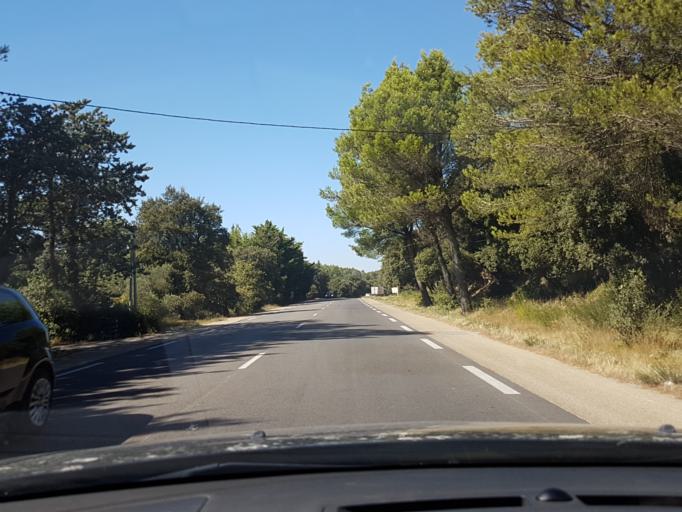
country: FR
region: Provence-Alpes-Cote d'Azur
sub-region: Departement des Bouches-du-Rhone
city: Orgon
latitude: 43.7994
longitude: 5.0278
